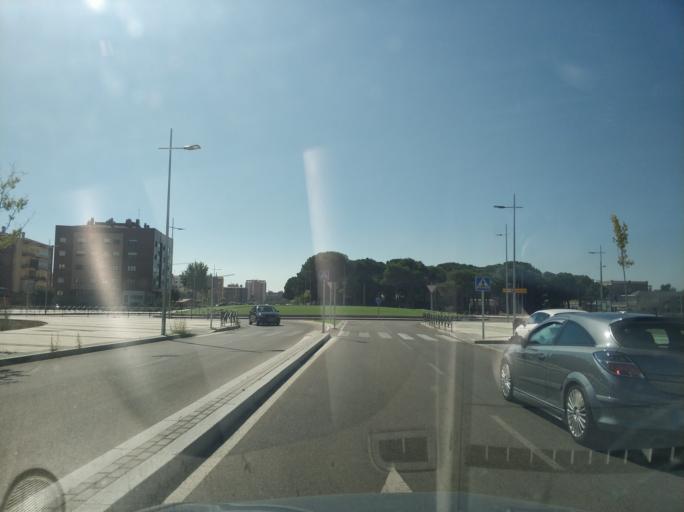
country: ES
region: Castille and Leon
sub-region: Provincia de Burgos
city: Aranda de Duero
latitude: 41.6692
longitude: -3.6939
